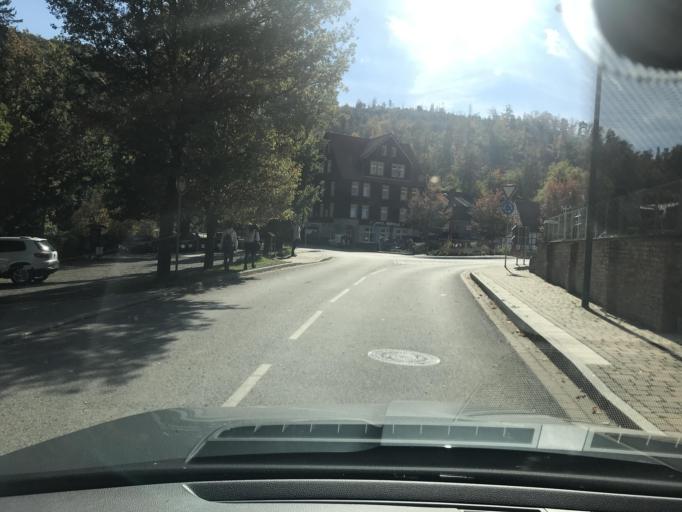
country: DE
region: Saxony-Anhalt
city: Timmenrode
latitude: 51.7165
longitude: 10.9741
